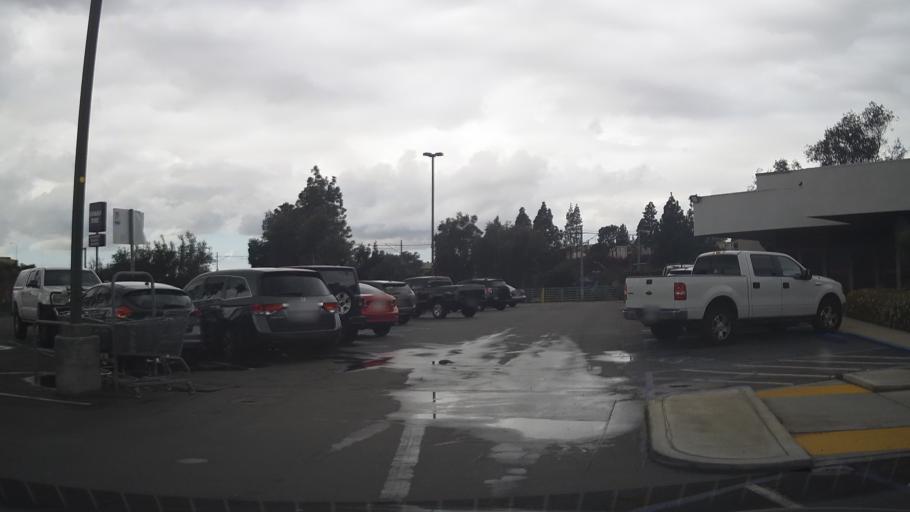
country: US
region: California
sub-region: San Diego County
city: La Mesa
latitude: 32.7773
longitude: -117.0160
